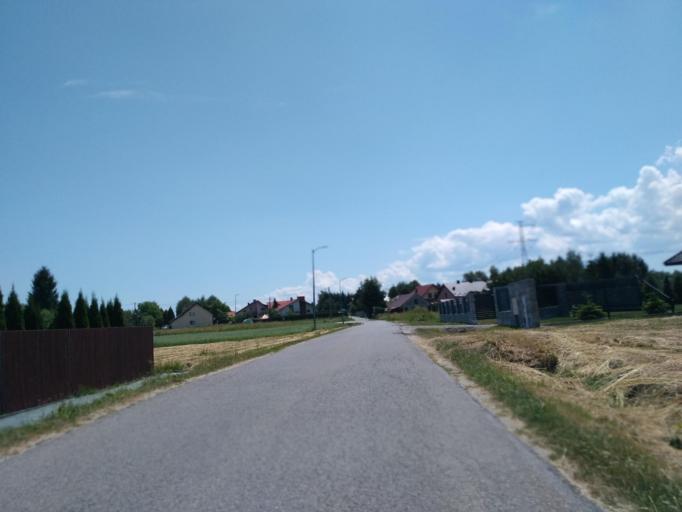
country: PL
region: Subcarpathian Voivodeship
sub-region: Powiat krosnienski
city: Korczyna
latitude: 49.7073
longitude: 21.7944
